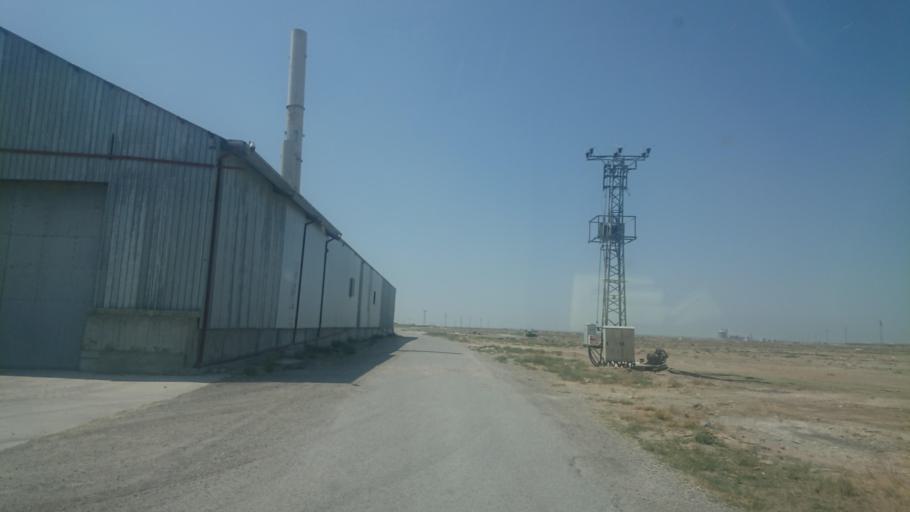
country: TR
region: Aksaray
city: Sultanhani
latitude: 38.2836
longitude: 33.7093
